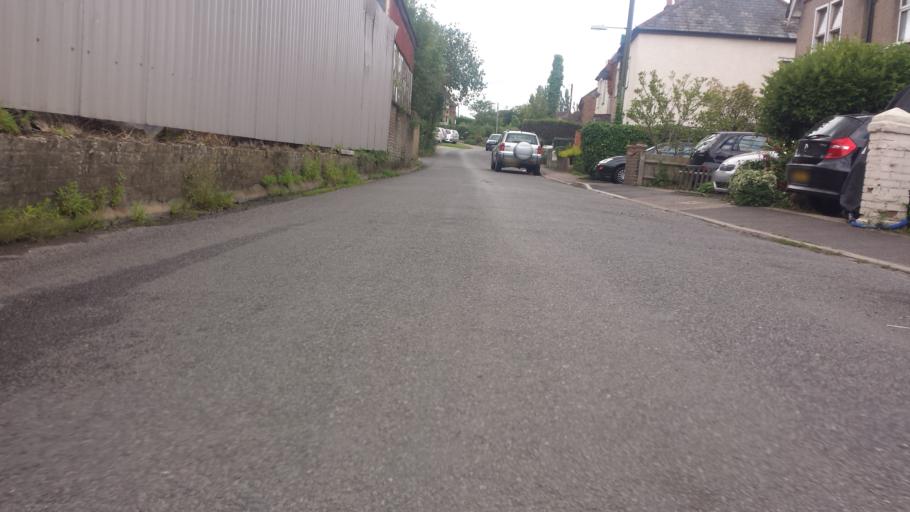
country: GB
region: England
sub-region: Kent
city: Swanley
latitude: 51.3828
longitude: 0.1569
